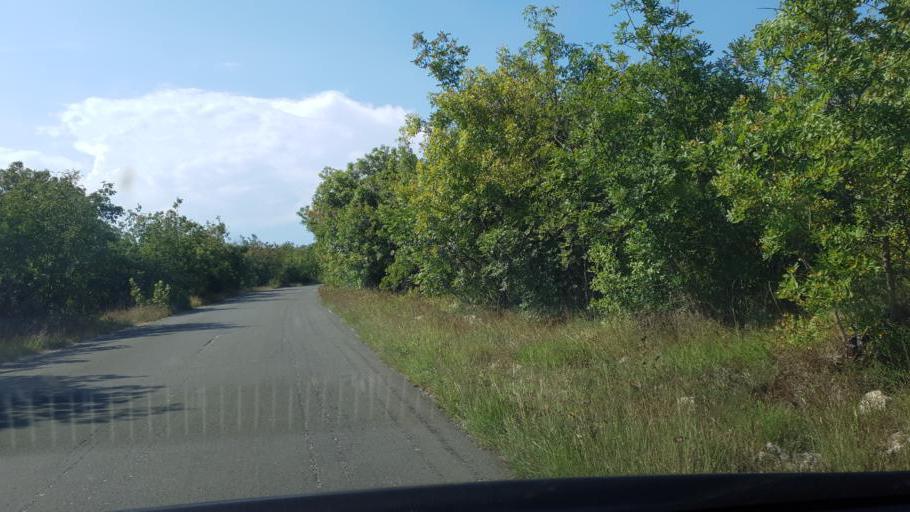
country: HR
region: Primorsko-Goranska
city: Omisalj
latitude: 45.1848
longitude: 14.5877
